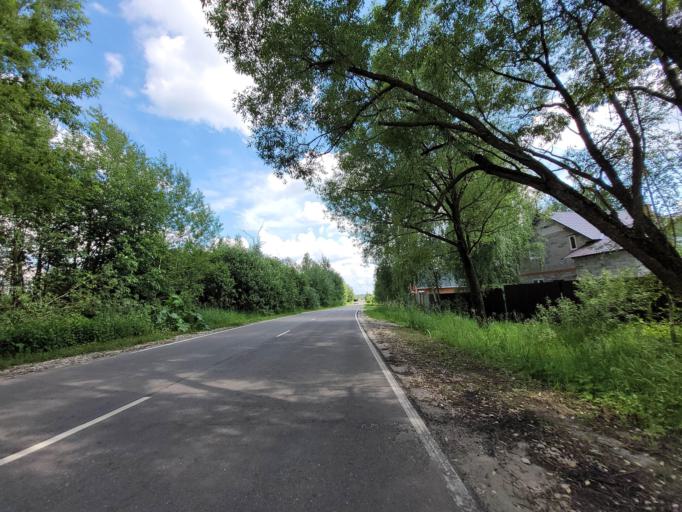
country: RU
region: Moskovskaya
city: Konobeyevo
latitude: 55.3980
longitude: 38.6811
